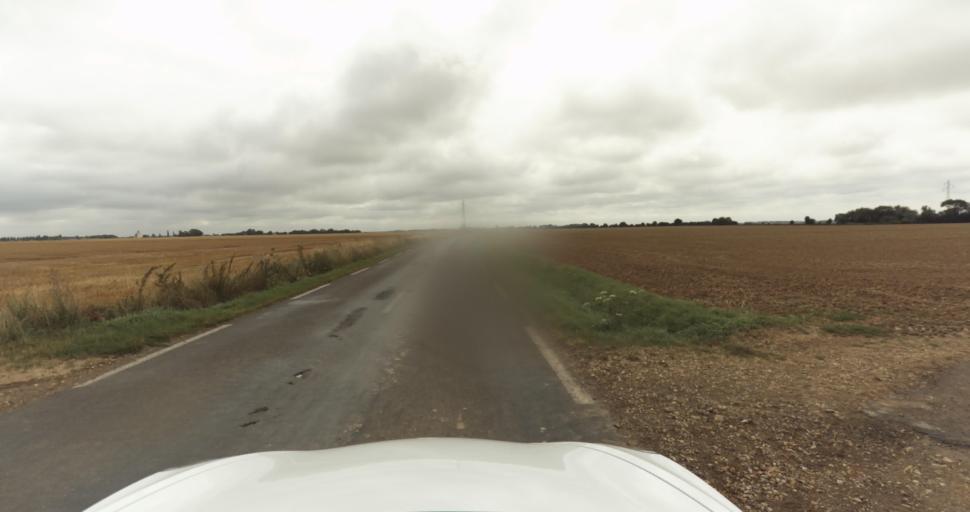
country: FR
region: Haute-Normandie
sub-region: Departement de l'Eure
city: Claville
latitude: 49.0844
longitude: 1.0513
